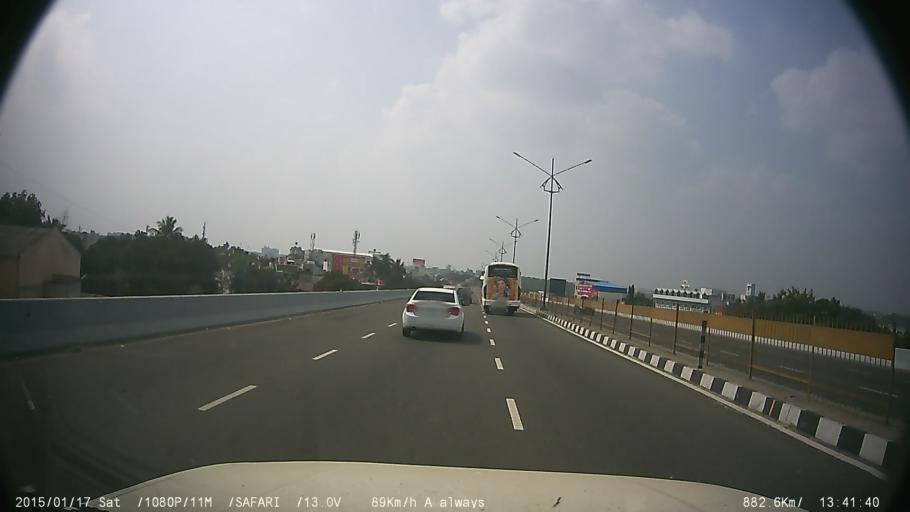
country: IN
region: Tamil Nadu
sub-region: Vellore
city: Vellore
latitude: 12.9349
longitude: 79.1510
